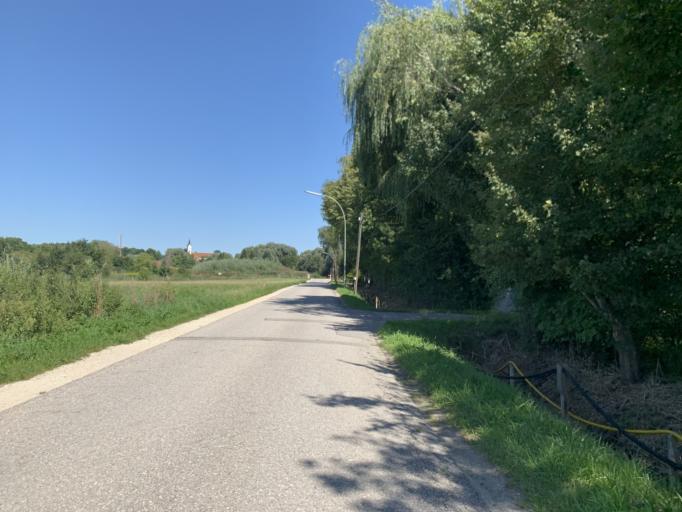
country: DE
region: Bavaria
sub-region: Upper Bavaria
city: Freising
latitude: 48.3908
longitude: 11.7182
